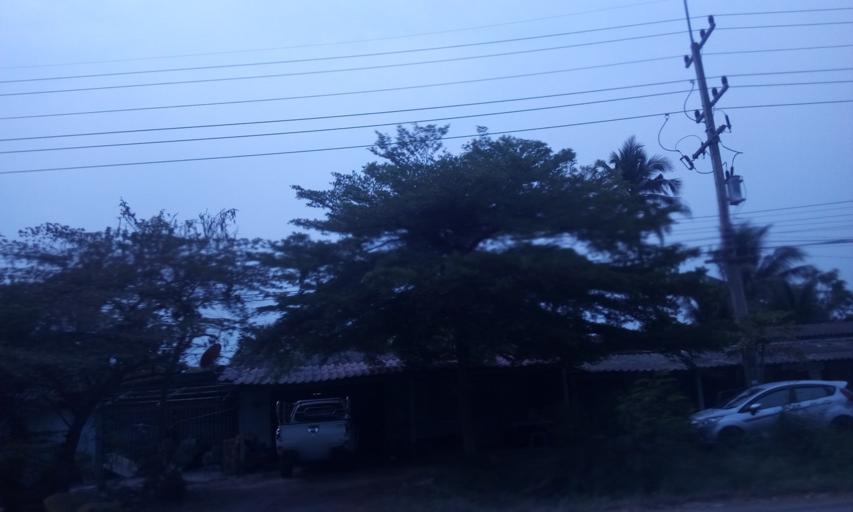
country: TH
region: Chon Buri
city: Ban Bueng
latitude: 13.2409
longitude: 101.2412
